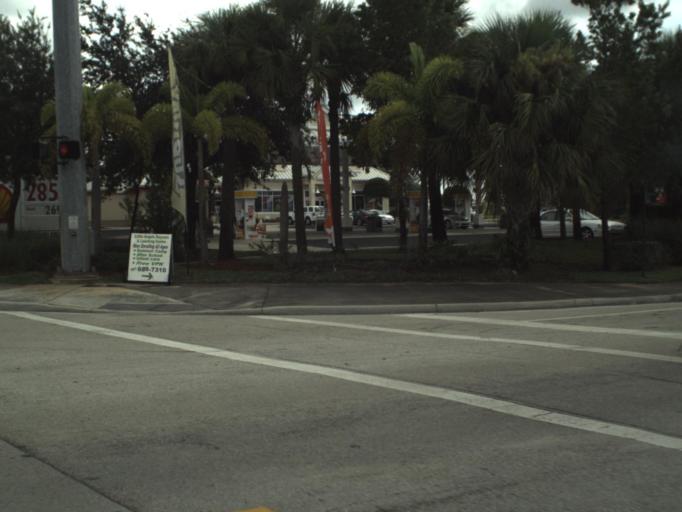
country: US
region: Florida
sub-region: Palm Beach County
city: Lake Clarke Shores
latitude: 26.6724
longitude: -80.0877
